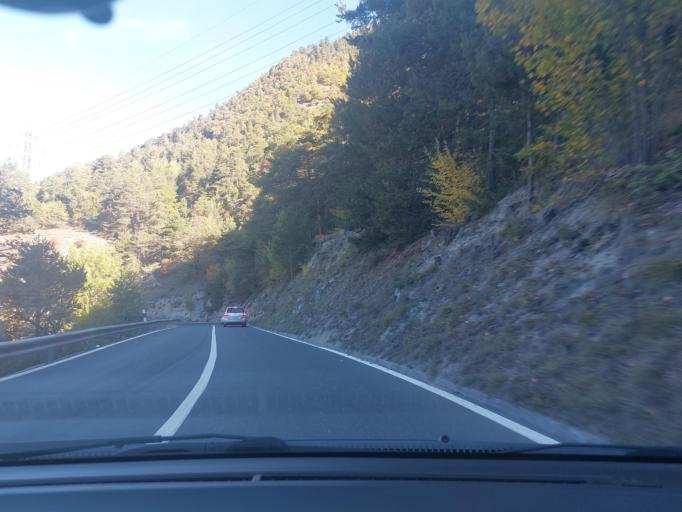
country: CH
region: Valais
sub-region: Sierre District
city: Chippis
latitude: 46.2670
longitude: 7.5563
